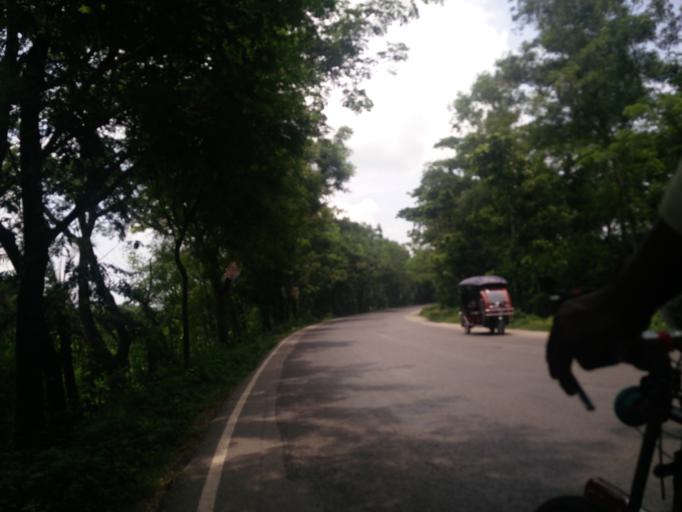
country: BD
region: Khulna
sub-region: Magura
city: Magura
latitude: 23.5457
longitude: 89.5189
